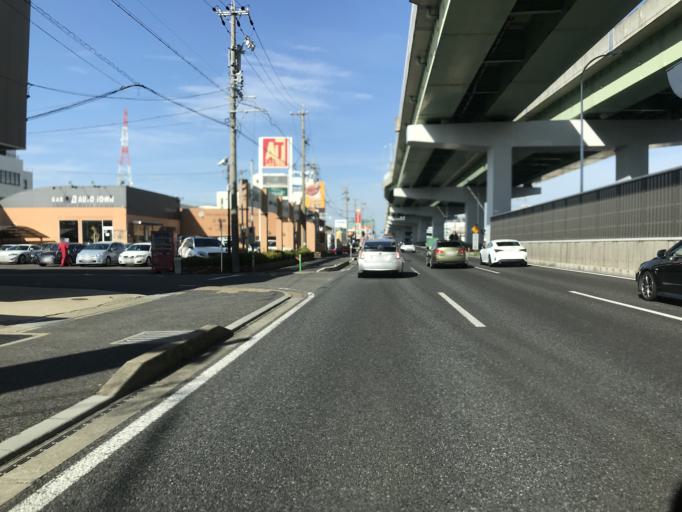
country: JP
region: Aichi
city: Iwakura
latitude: 35.2493
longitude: 136.8443
